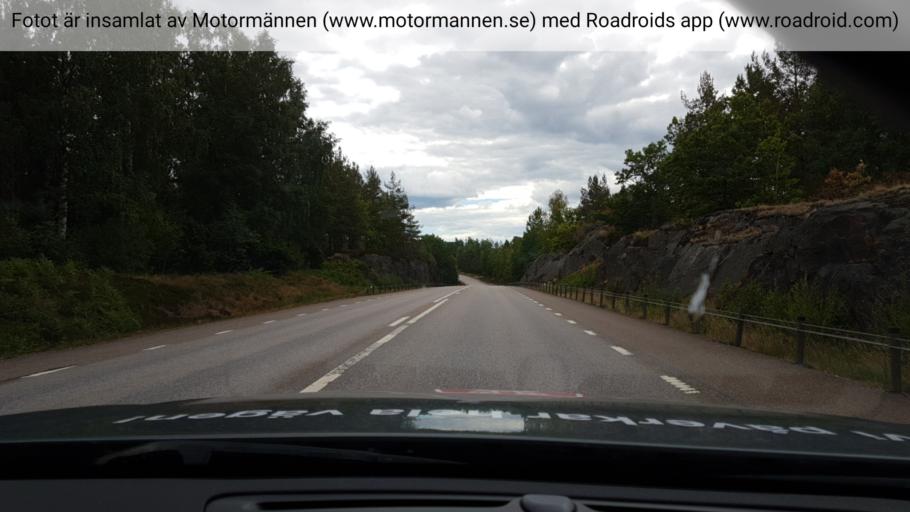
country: SE
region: Kalmar
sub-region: Oskarshamns Kommun
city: Oskarshamn
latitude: 57.5067
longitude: 16.5023
